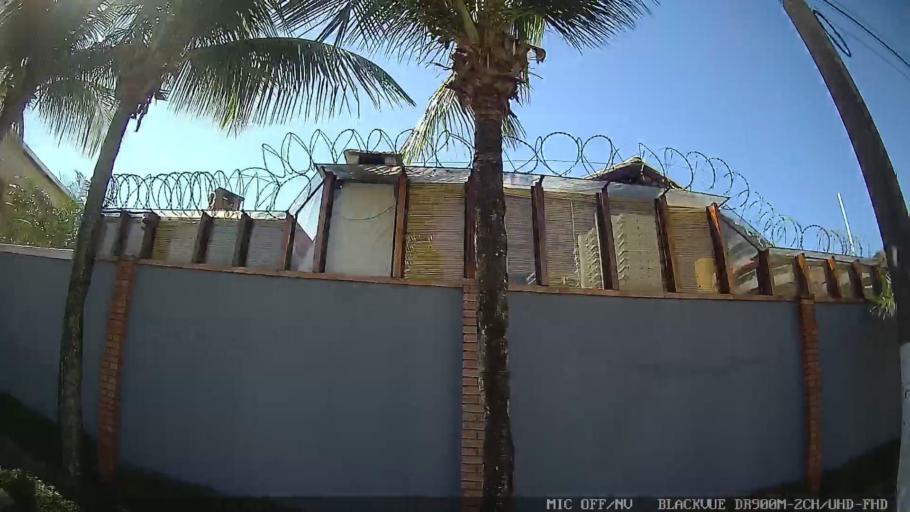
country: BR
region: Sao Paulo
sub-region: Guaruja
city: Guaruja
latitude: -23.9831
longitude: -46.2293
